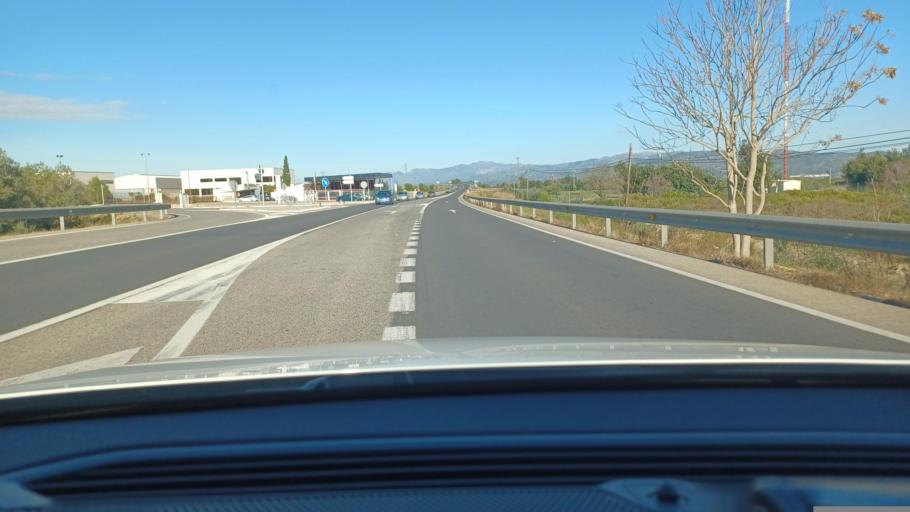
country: ES
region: Catalonia
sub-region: Provincia de Tarragona
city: Santa Barbara
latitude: 40.7357
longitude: 0.5034
